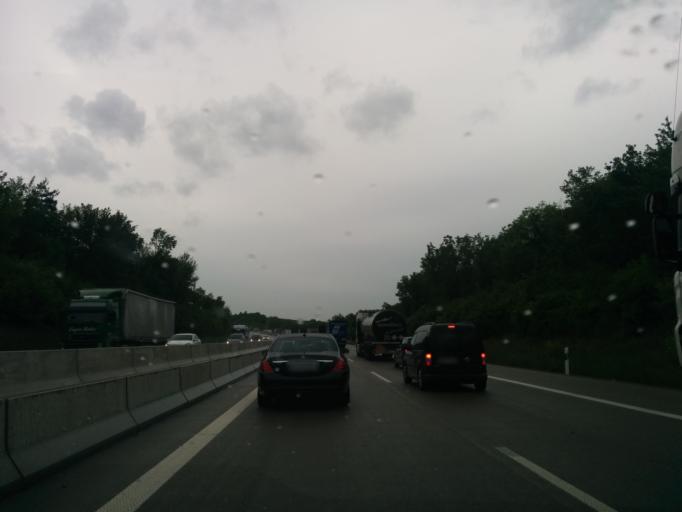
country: DE
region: Bavaria
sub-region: Regierungsbezirk Unterfranken
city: Obernbreit
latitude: 49.6427
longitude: 10.1668
